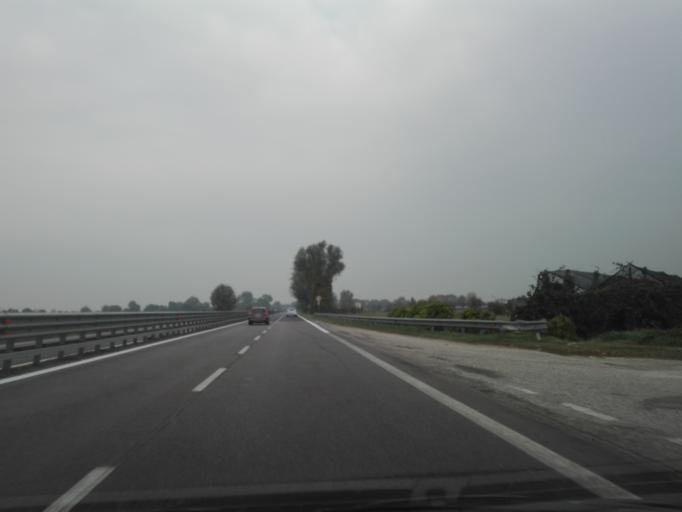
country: IT
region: Veneto
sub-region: Provincia di Verona
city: Villa Bartolomea
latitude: 45.1570
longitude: 11.3198
